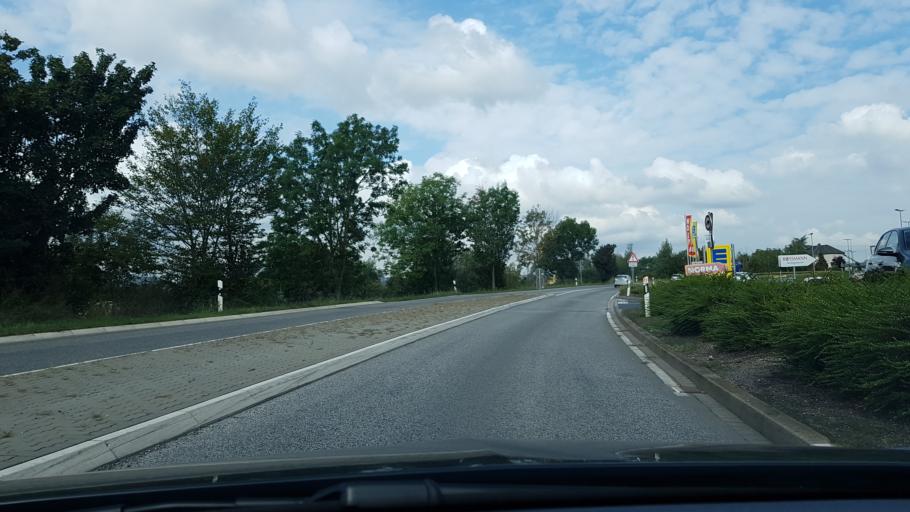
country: DE
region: Rheinland-Pfalz
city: Plaidt
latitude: 50.3882
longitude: 7.3828
